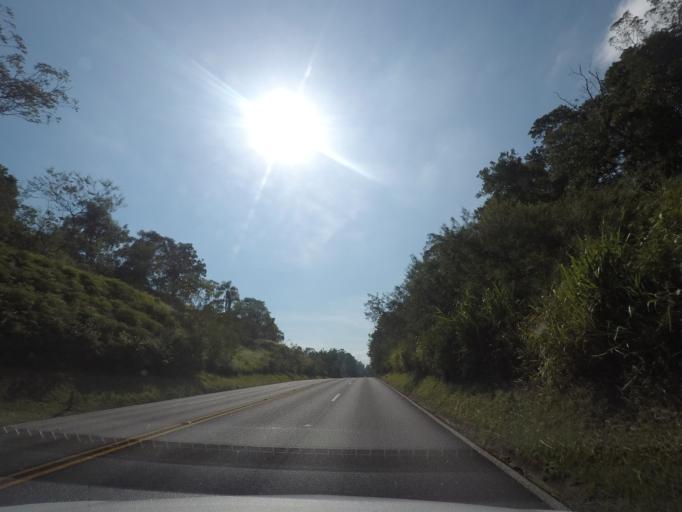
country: BR
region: Parana
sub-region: Pontal Do Parana
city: Pontal do Parana
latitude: -25.6081
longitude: -48.6063
